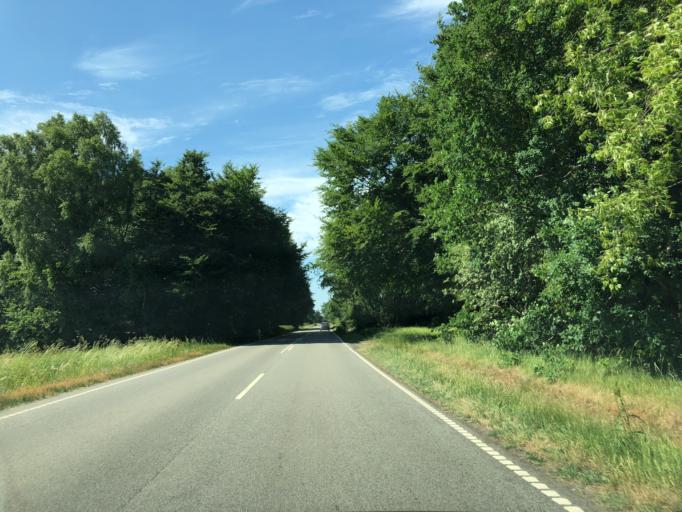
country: DK
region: Central Jutland
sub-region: Ikast-Brande Kommune
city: Brande
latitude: 55.9184
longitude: 9.1694
